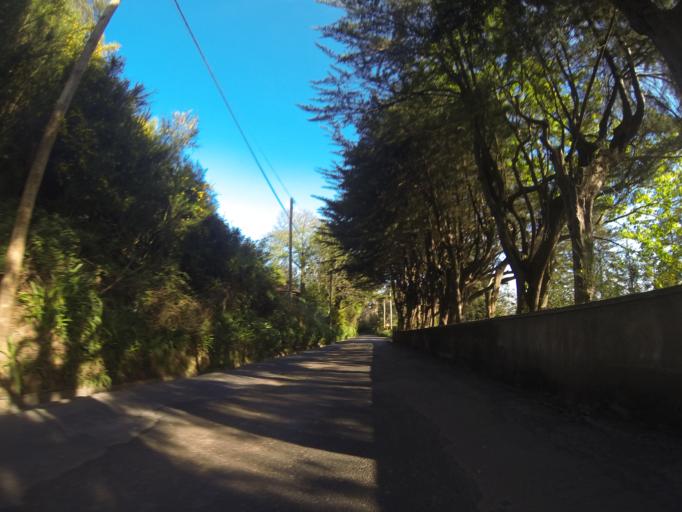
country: PT
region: Madeira
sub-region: Santa Cruz
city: Camacha
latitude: 32.6875
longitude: -16.8734
